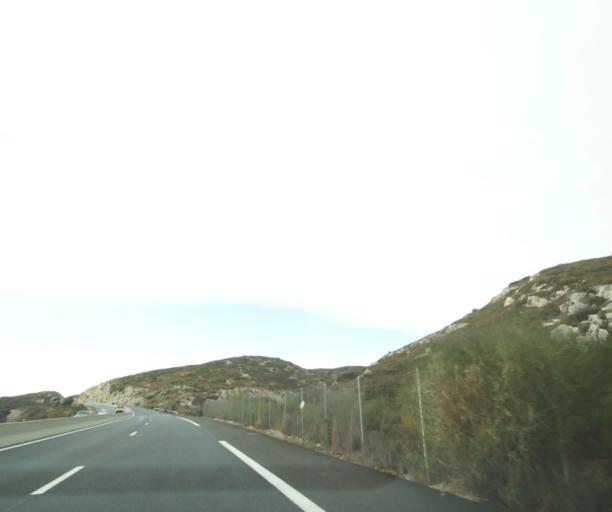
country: FR
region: Provence-Alpes-Cote d'Azur
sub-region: Departement des Bouches-du-Rhone
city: Carry-le-Rouet
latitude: 43.3407
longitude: 5.1498
